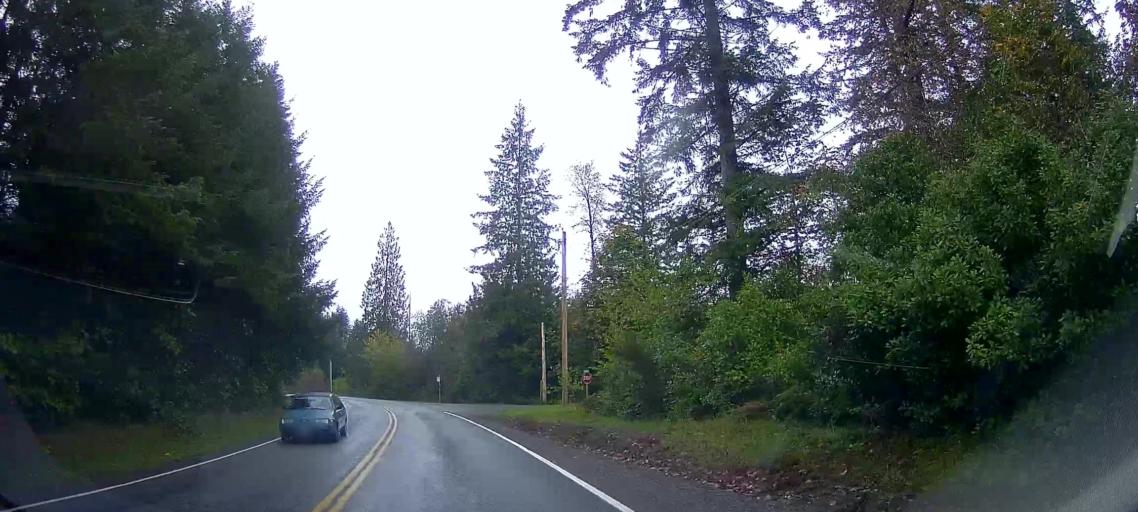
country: US
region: Washington
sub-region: Snohomish County
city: Darrington
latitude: 48.5279
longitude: -121.7666
